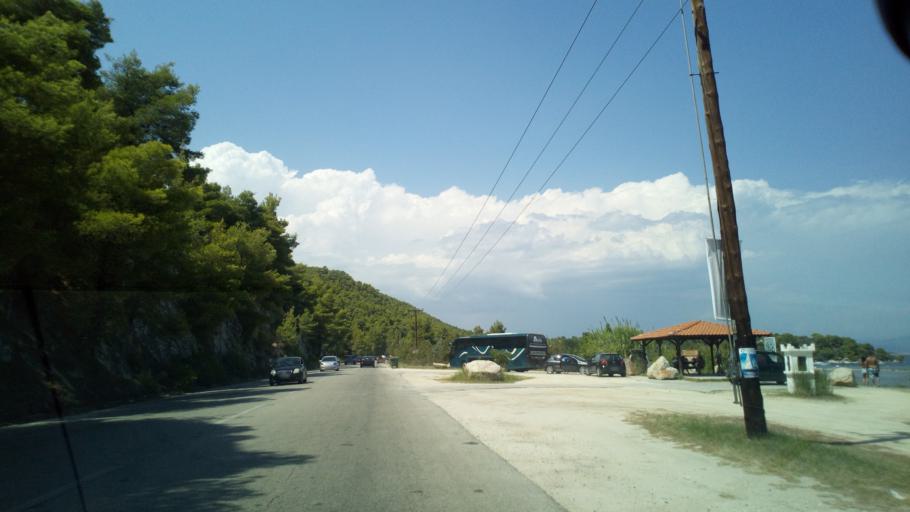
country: GR
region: Central Macedonia
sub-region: Nomos Chalkidikis
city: Agios Nikolaos
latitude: 40.1999
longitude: 23.7651
